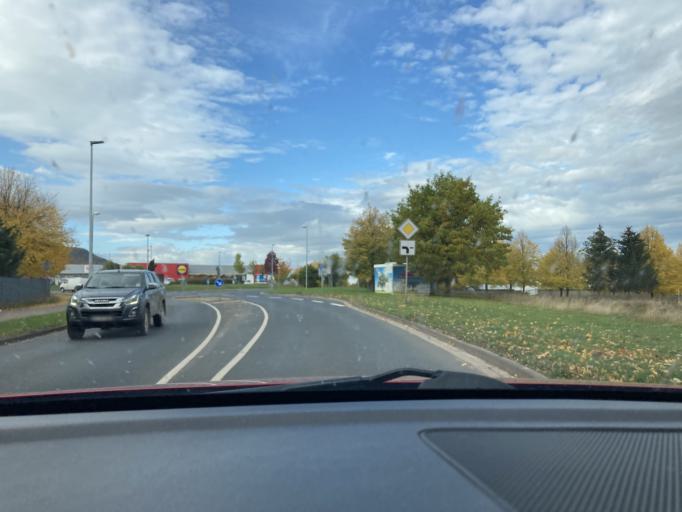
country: DE
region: Thuringia
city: Bleicherode
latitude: 51.4497
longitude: 10.5730
